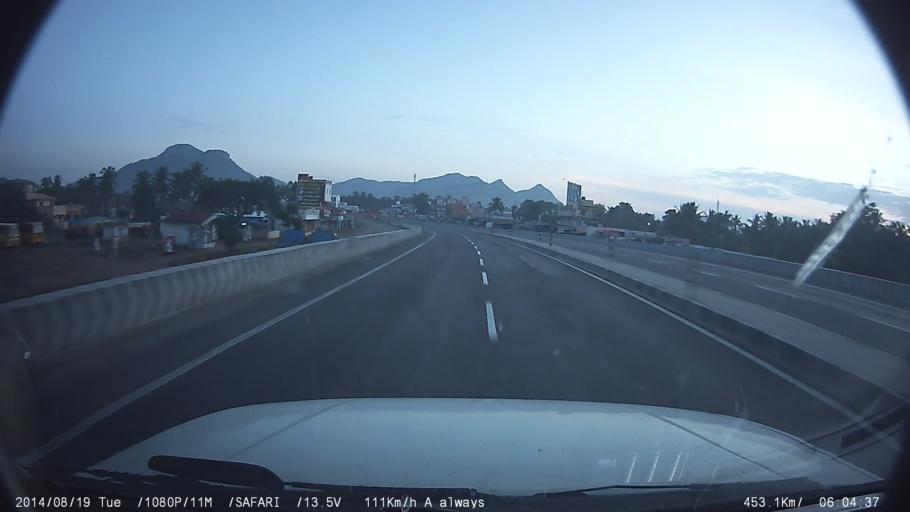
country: IN
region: Tamil Nadu
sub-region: Salem
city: Omalur
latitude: 11.8669
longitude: 78.0834
